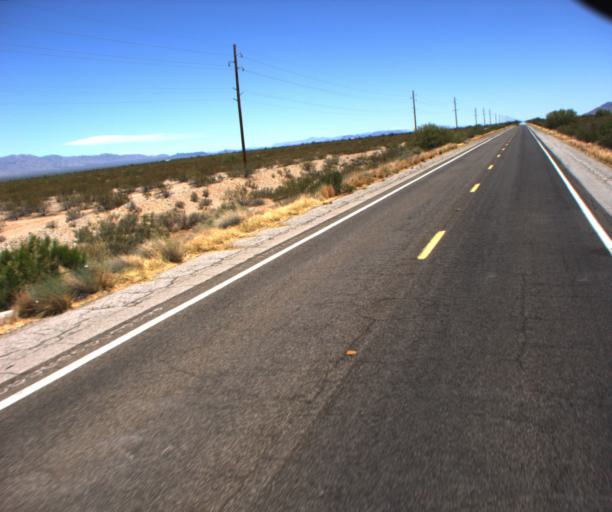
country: US
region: Arizona
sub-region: La Paz County
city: Salome
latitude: 33.8454
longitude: -113.4646
